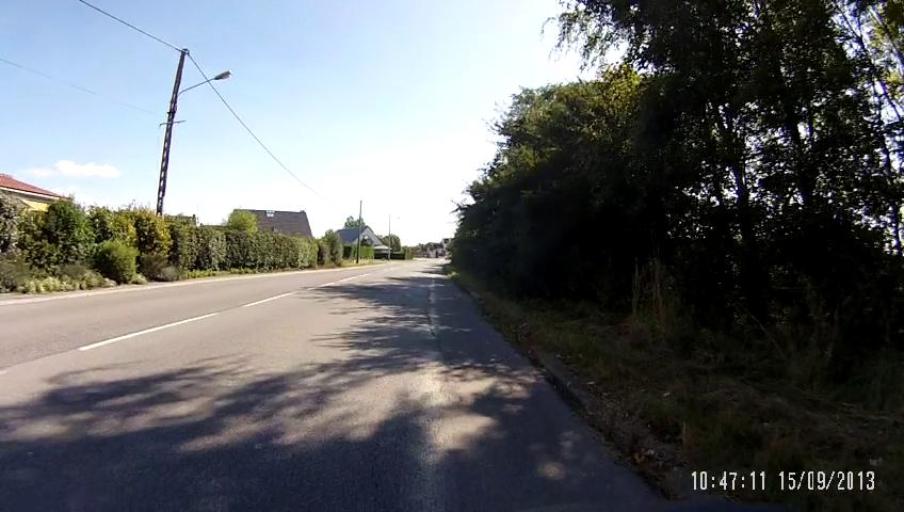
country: FR
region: Nord-Pas-de-Calais
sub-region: Departement du Nord
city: Leffrinckoucke
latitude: 51.0480
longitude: 2.4422
